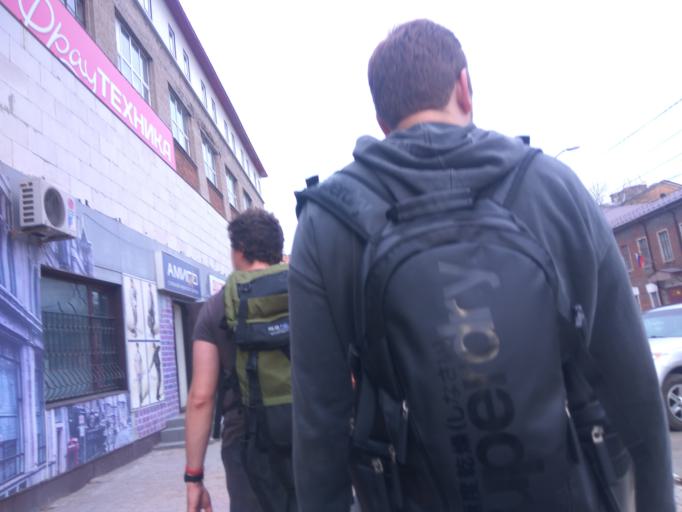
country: RU
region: Vladimir
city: Aleksandrov
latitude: 56.3976
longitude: 38.7175
